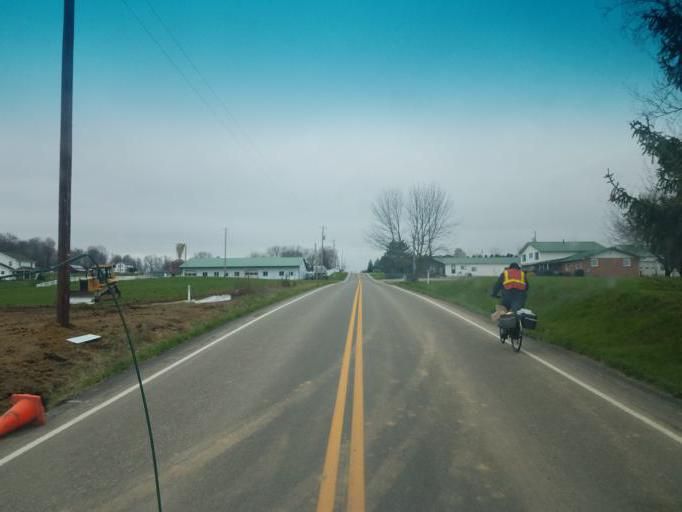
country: US
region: Ohio
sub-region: Tuscarawas County
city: Sugarcreek
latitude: 40.6187
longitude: -81.7367
